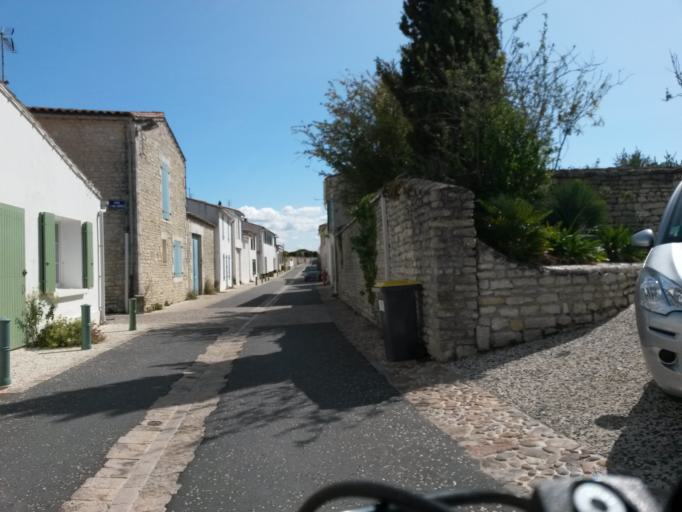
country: FR
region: Poitou-Charentes
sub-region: Departement de la Charente-Maritime
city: La Flotte
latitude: 46.1899
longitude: -1.3354
